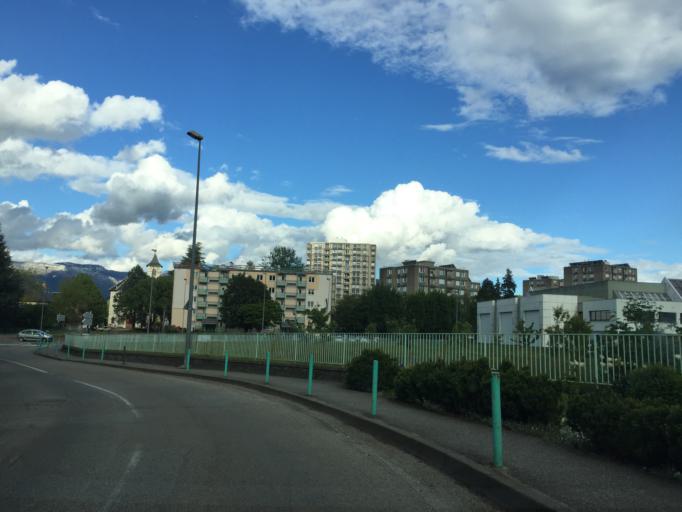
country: FR
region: Rhone-Alpes
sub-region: Departement de la Savoie
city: Cognin
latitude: 45.5622
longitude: 5.8925
